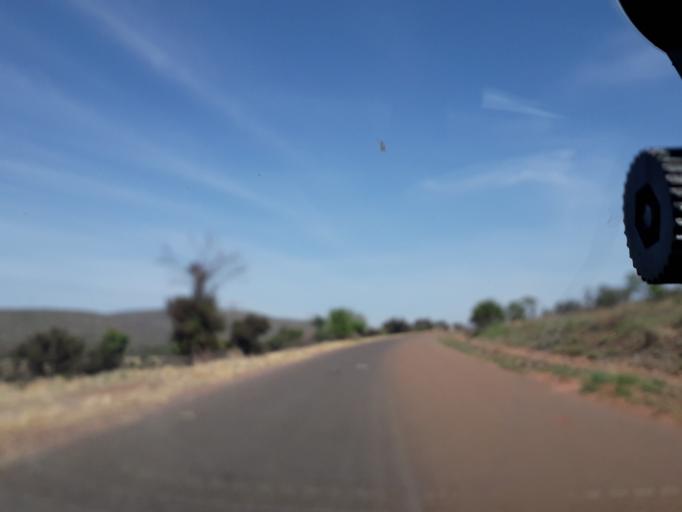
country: ZA
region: Limpopo
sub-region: Waterberg District Municipality
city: Warmbaths
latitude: -24.8293
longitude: 28.2192
